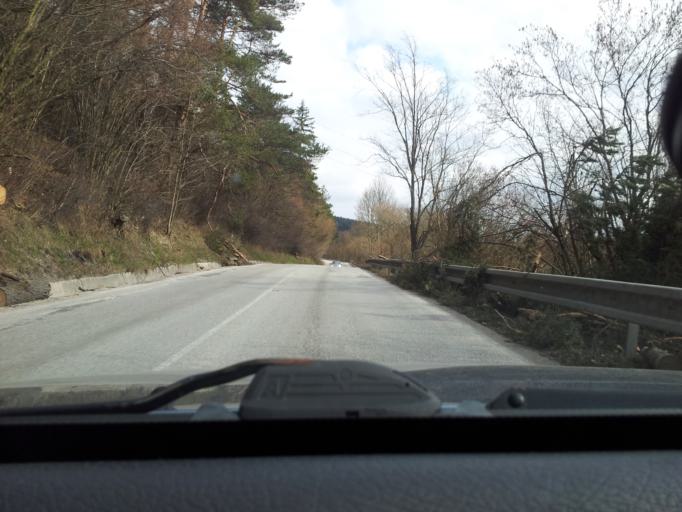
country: SK
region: Banskobystricky
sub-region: Okres Ziar nad Hronom
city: Kremnica
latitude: 48.7755
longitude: 18.8895
